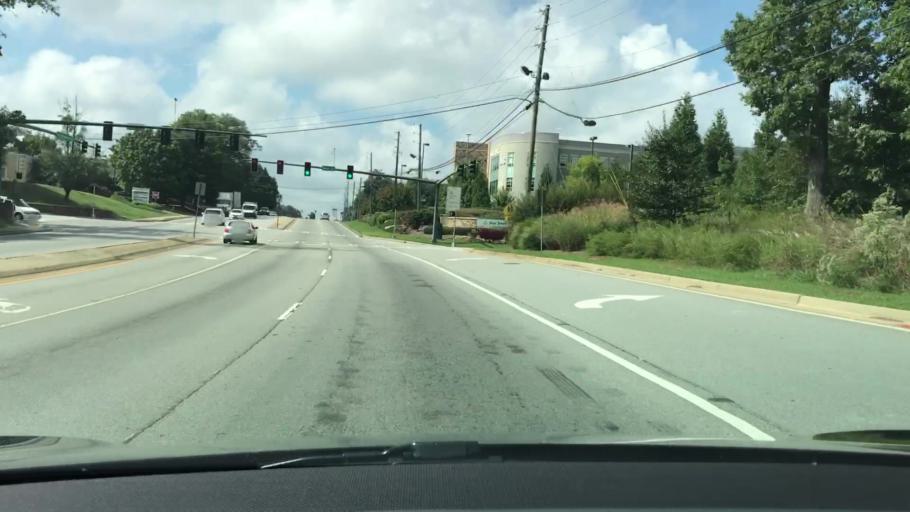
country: US
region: Georgia
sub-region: Hall County
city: Gainesville
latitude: 34.3061
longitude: -83.8098
